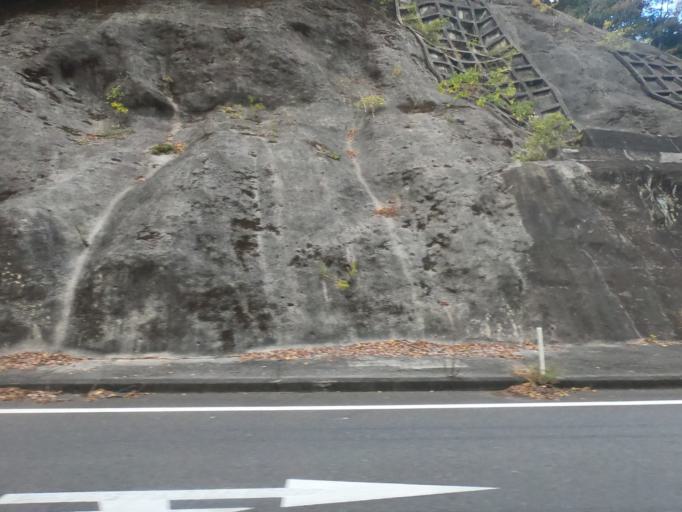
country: JP
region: Kumamoto
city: Minamata
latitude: 32.2568
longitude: 130.5091
